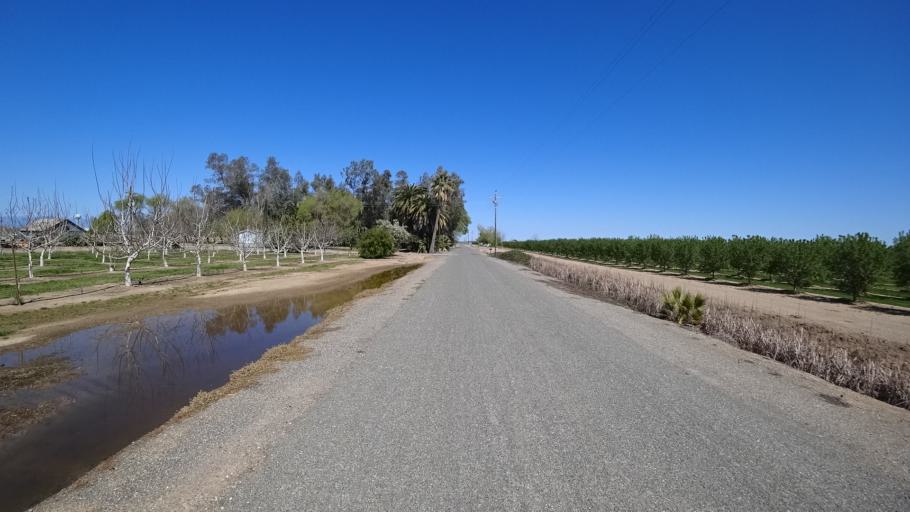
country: US
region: California
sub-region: Glenn County
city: Orland
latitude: 39.6767
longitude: -122.2343
